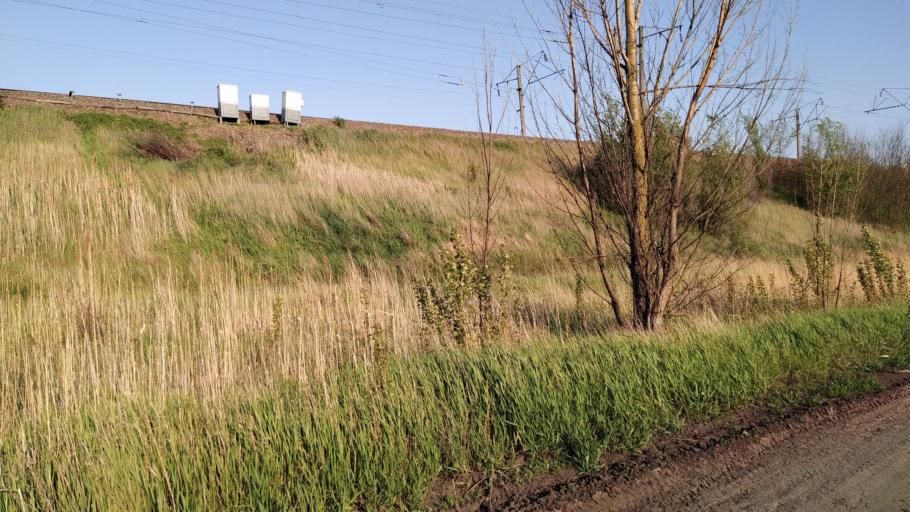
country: RU
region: Rostov
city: Bataysk
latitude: 47.0912
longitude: 39.7126
